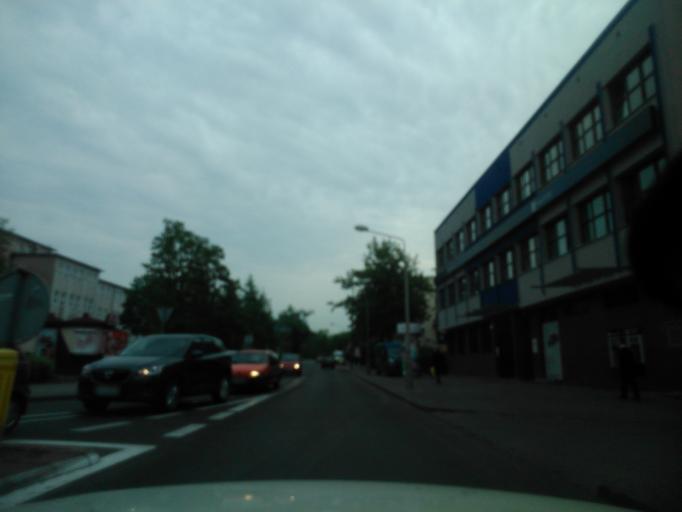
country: PL
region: Kujawsko-Pomorskie
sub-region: Torun
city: Torun
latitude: 53.0163
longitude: 18.6021
